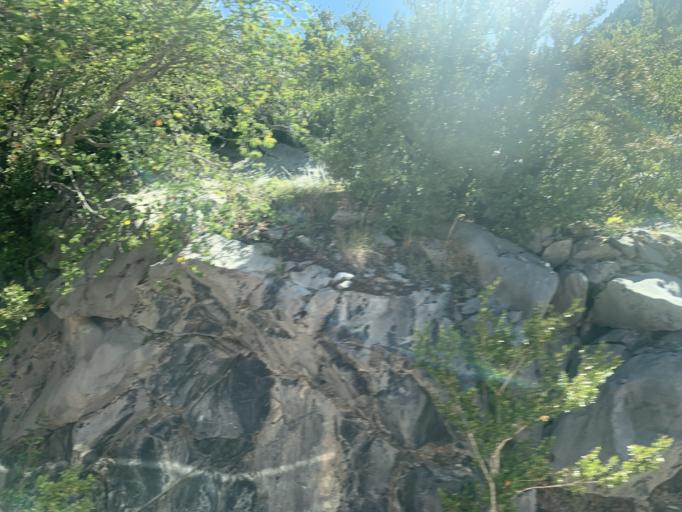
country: ES
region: Aragon
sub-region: Provincia de Huesca
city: Broto
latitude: 42.6519
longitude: -0.1000
